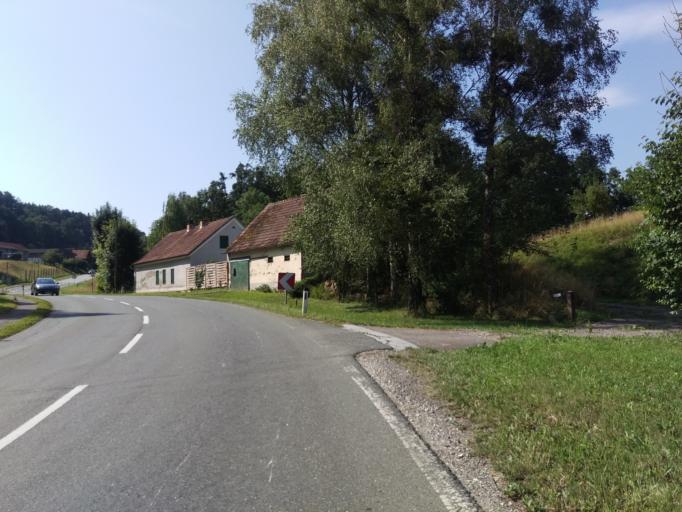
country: AT
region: Styria
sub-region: Politischer Bezirk Graz-Umgebung
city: Mellach
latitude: 46.9399
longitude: 15.5102
